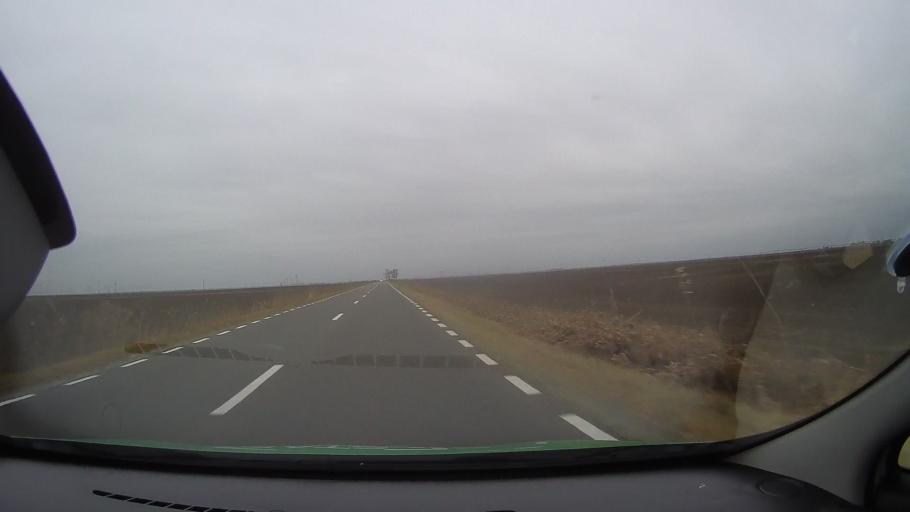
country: RO
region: Ialomita
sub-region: Comuna Gheorghe Lazar
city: Gheorghe Lazar
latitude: 44.6633
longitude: 27.4143
